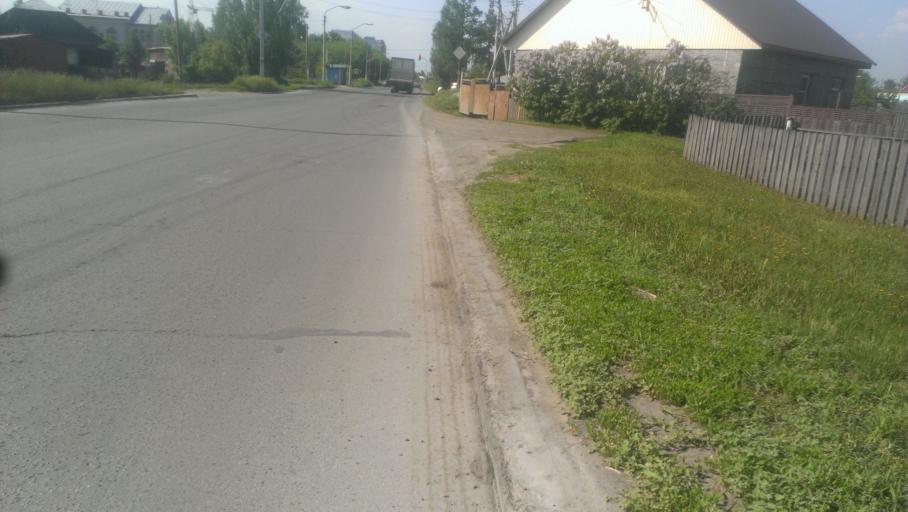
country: RU
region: Altai Krai
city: Novoaltaysk
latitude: 53.4059
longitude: 83.9447
